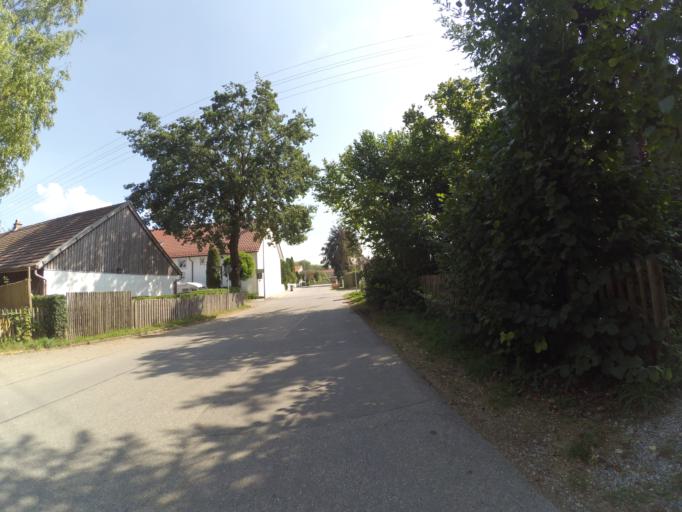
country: DE
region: Bavaria
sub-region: Swabia
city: Lamerdingen
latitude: 48.1041
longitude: 10.7697
